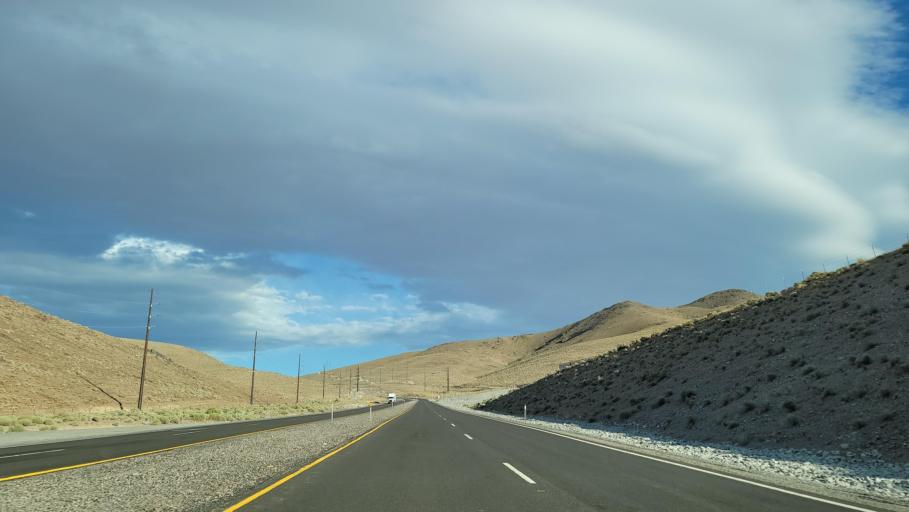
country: US
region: Nevada
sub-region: Lyon County
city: Stagecoach
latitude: 39.5180
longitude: -119.4729
